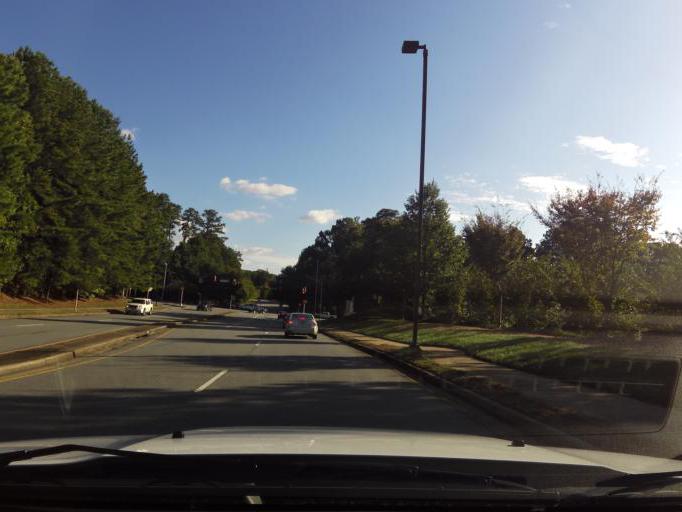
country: US
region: Georgia
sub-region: Cobb County
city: Kennesaw
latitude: 34.0054
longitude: -84.5866
